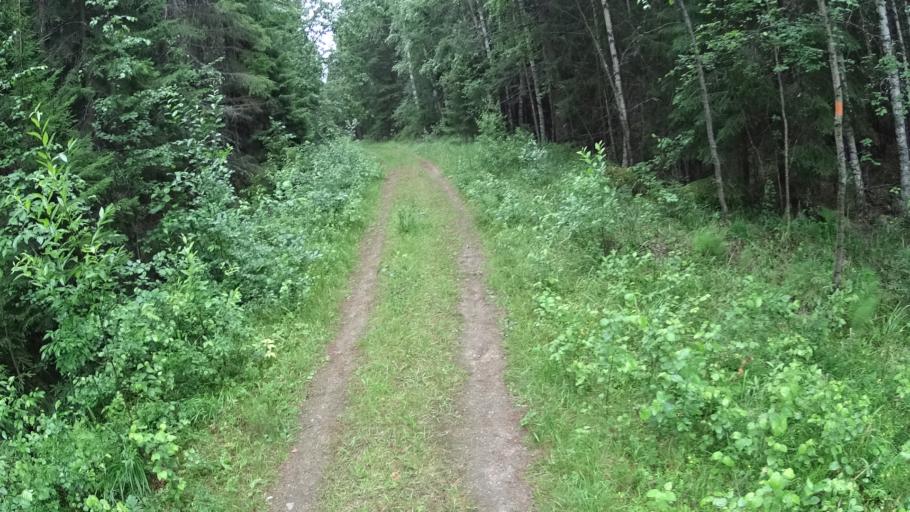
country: FI
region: Southern Savonia
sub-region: Mikkeli
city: Maentyharju
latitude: 61.1875
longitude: 26.8267
